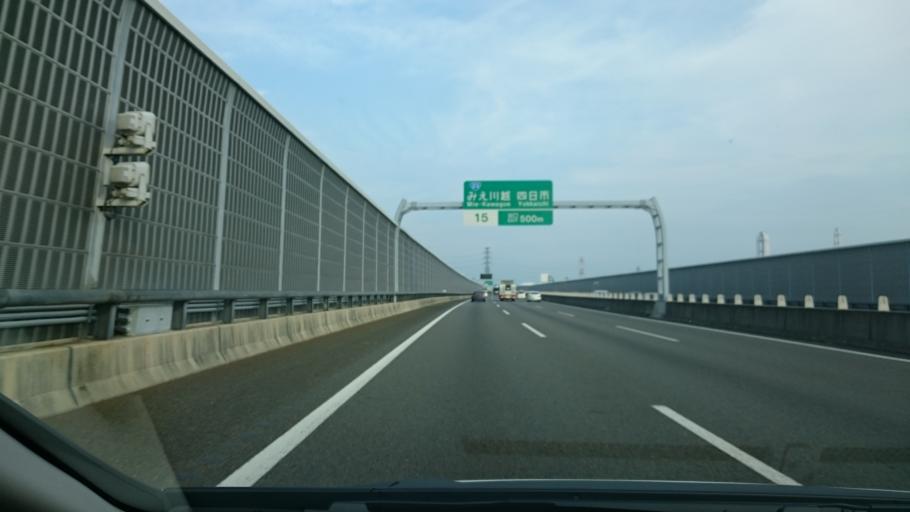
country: JP
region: Mie
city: Yokkaichi
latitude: 35.0263
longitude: 136.6776
